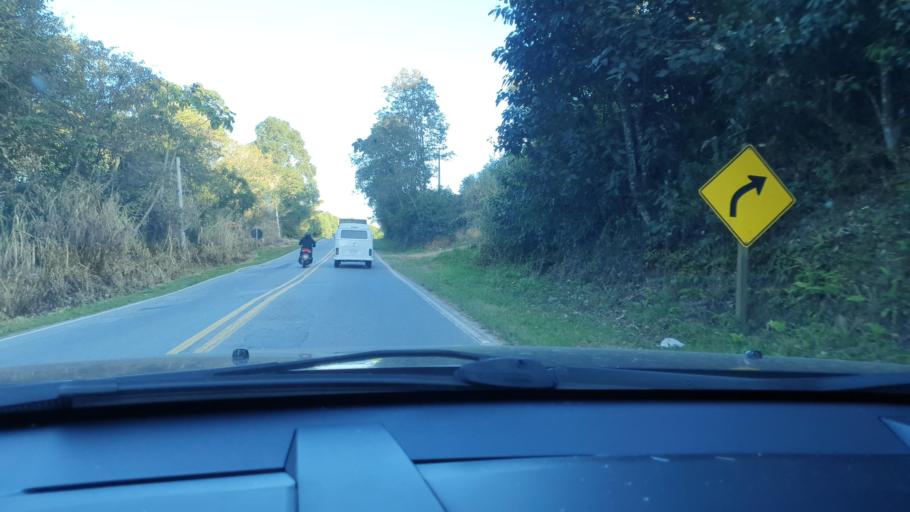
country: BR
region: Sao Paulo
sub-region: Piedade
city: Piedade
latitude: -23.7156
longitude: -47.3687
